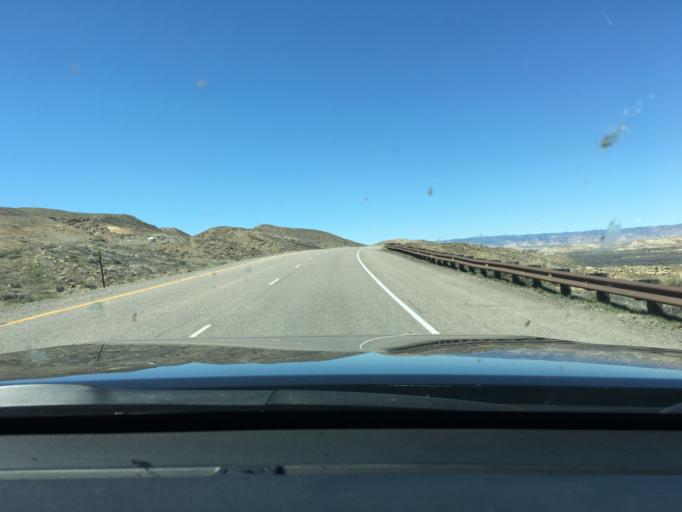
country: US
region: Colorado
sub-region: Mesa County
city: Loma
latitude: 39.2254
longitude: -108.8956
